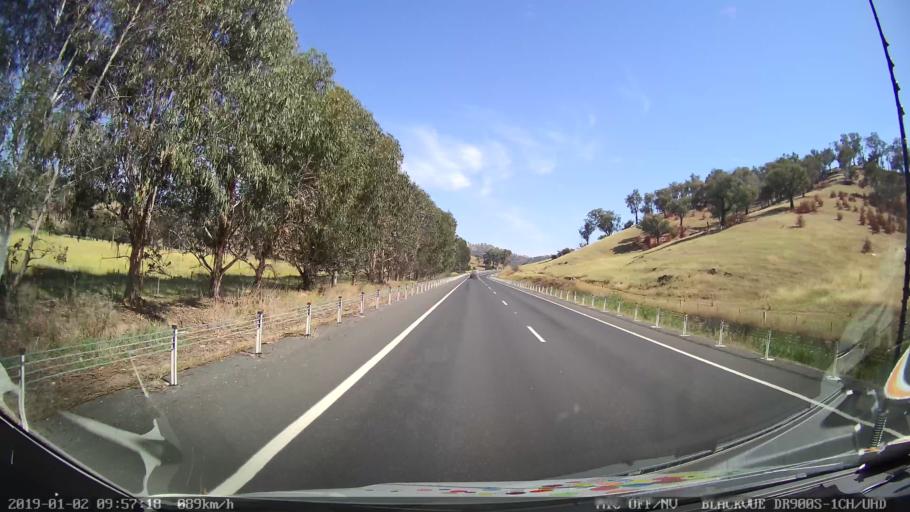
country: AU
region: New South Wales
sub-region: Tumut Shire
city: Tumut
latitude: -35.2073
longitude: 148.1669
